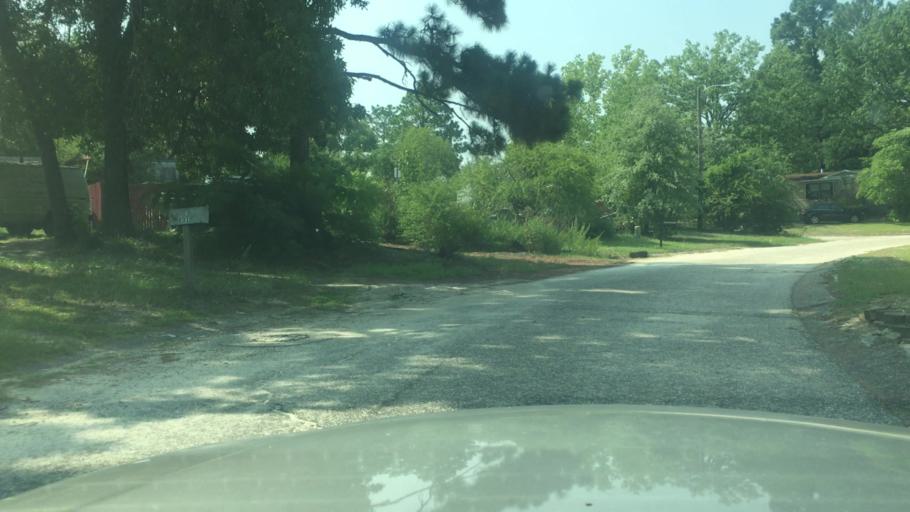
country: US
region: North Carolina
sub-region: Cumberland County
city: Hope Mills
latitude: 35.0038
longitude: -78.9506
